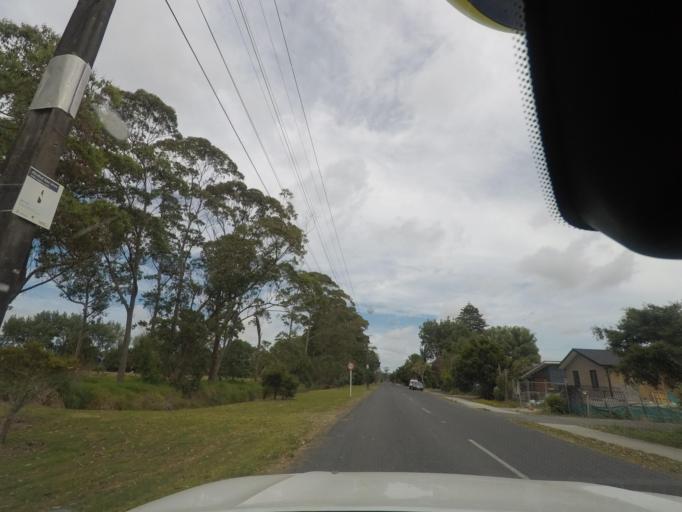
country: NZ
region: Auckland
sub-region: Auckland
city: Parakai
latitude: -36.6581
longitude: 174.4365
